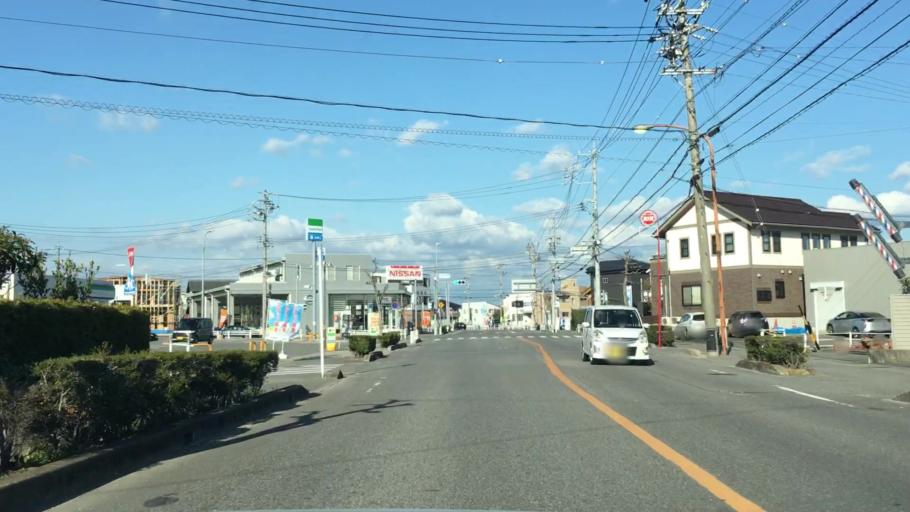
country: JP
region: Aichi
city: Nishio
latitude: 34.8535
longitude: 137.0623
